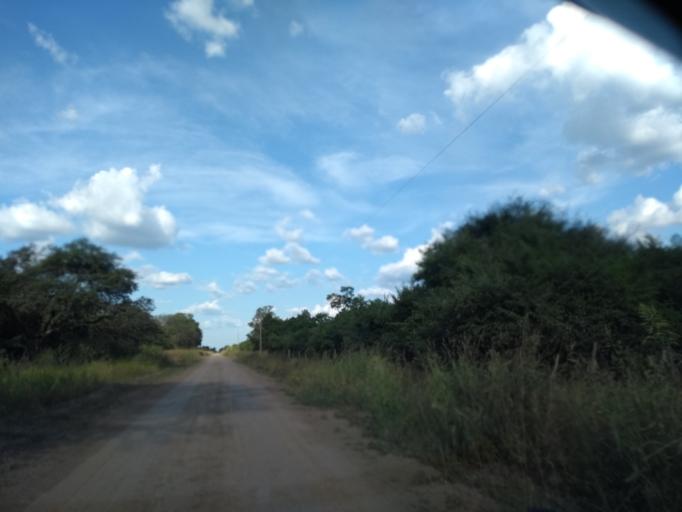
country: AR
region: Chaco
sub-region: Departamento de Quitilipi
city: Quitilipi
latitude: -26.7486
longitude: -60.2671
